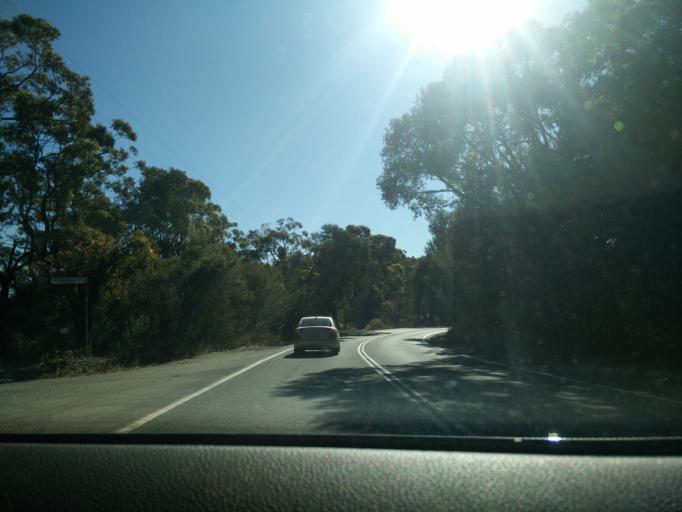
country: AU
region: New South Wales
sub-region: Hornsby Shire
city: Berowra
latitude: -33.5987
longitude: 151.1653
